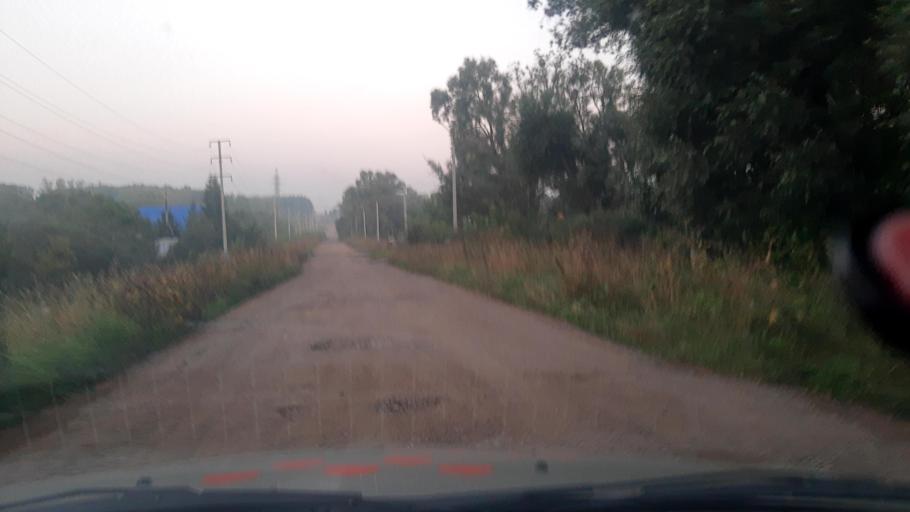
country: RU
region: Bashkortostan
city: Blagoveshchensk
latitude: 55.0506
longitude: 55.9818
